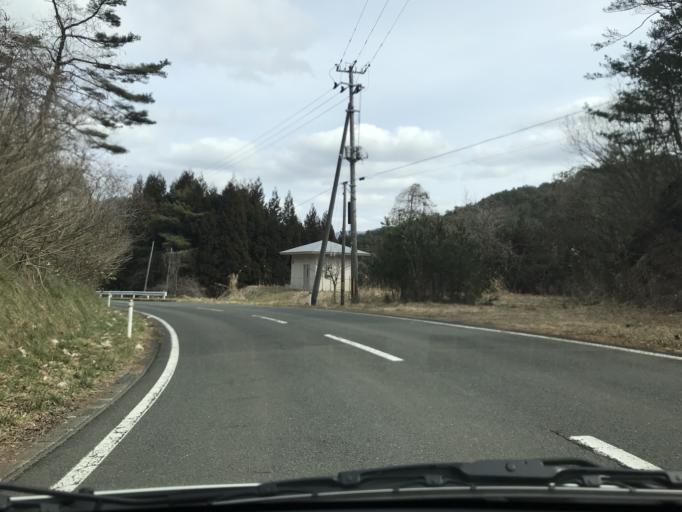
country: JP
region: Iwate
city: Kitakami
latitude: 39.2841
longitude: 141.3211
